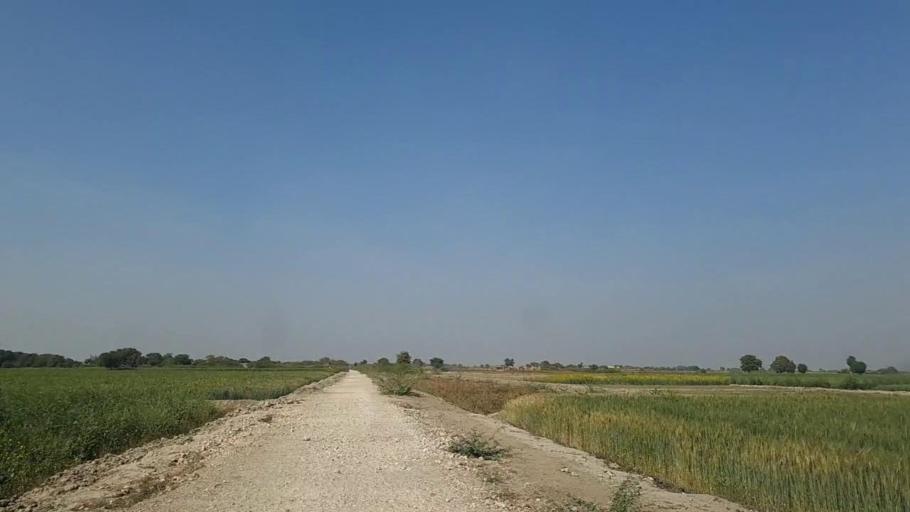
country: PK
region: Sindh
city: Naukot
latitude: 24.9422
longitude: 69.4839
